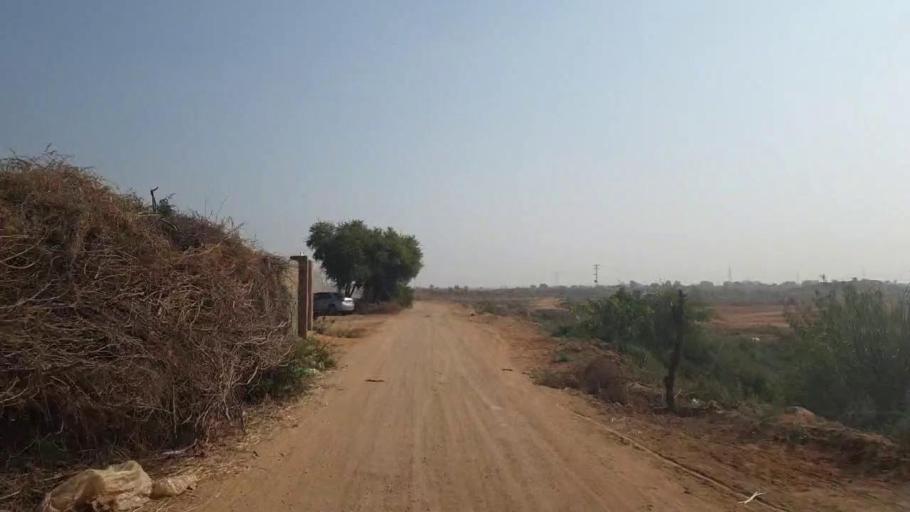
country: PK
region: Sindh
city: Jamshoro
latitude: 25.4617
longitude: 68.2909
